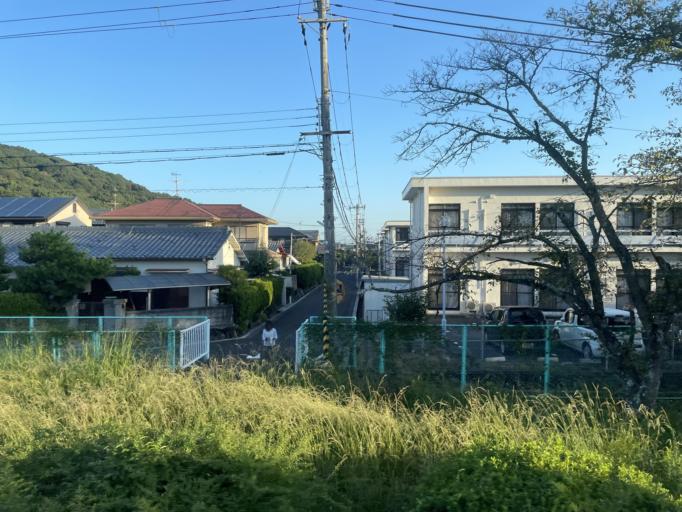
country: JP
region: Nara
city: Kashihara-shi
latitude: 34.5120
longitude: 135.8090
